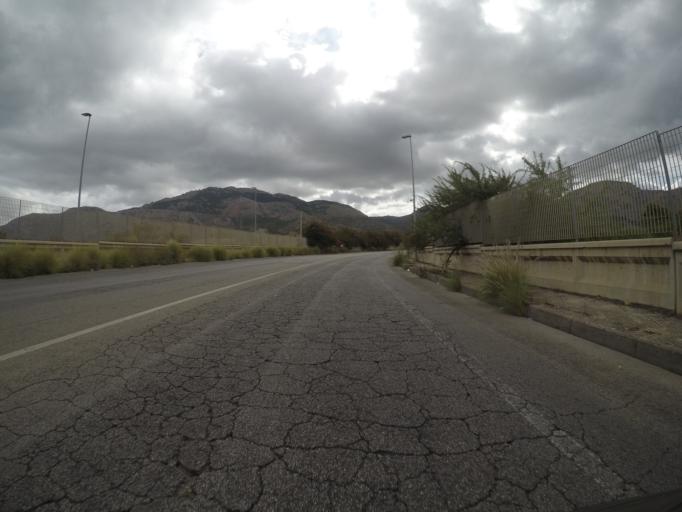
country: IT
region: Sicily
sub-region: Palermo
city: Capaci
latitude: 38.1728
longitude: 13.2187
